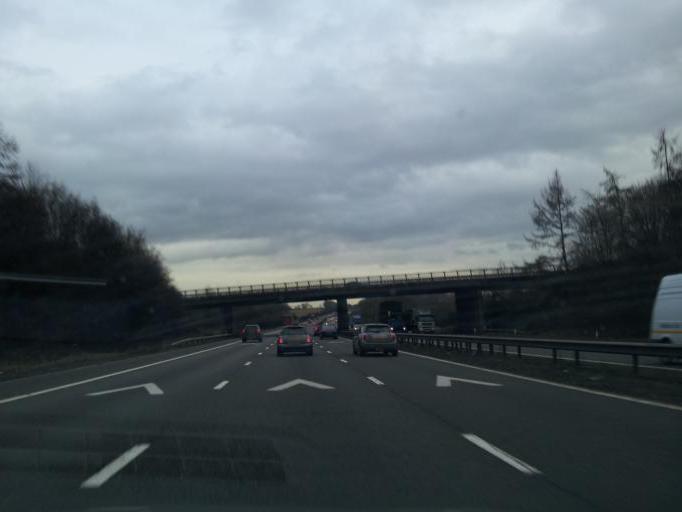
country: GB
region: England
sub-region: Warwickshire
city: Long Lawford
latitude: 52.4319
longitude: -1.3334
